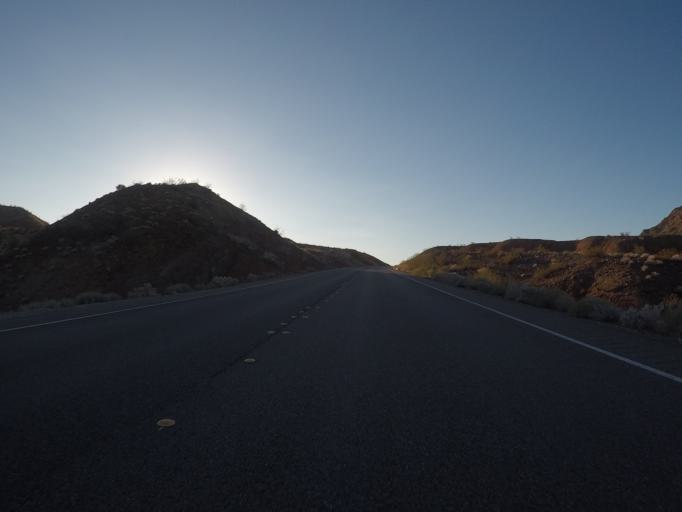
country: US
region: Nevada
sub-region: Clark County
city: Moapa Valley
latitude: 36.2441
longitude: -114.5044
